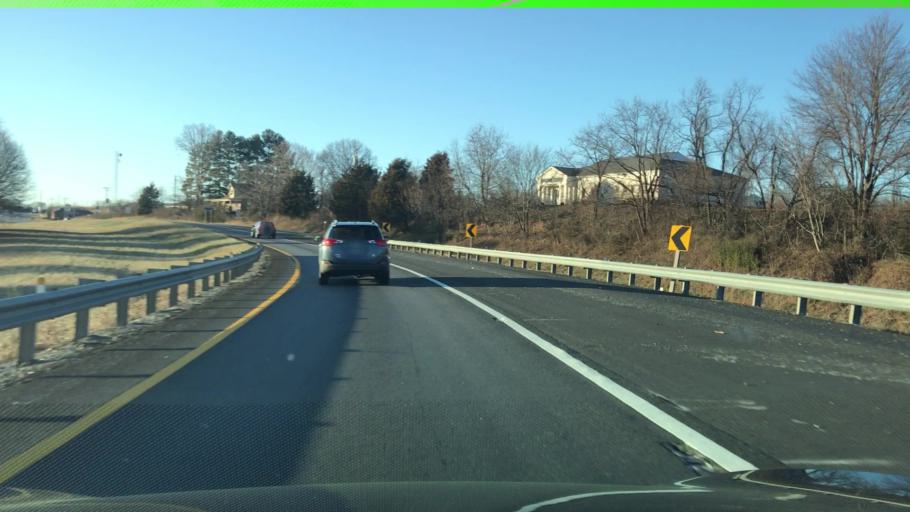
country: US
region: Virginia
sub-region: City of Bedford
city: Bedford
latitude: 37.3366
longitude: -79.5448
